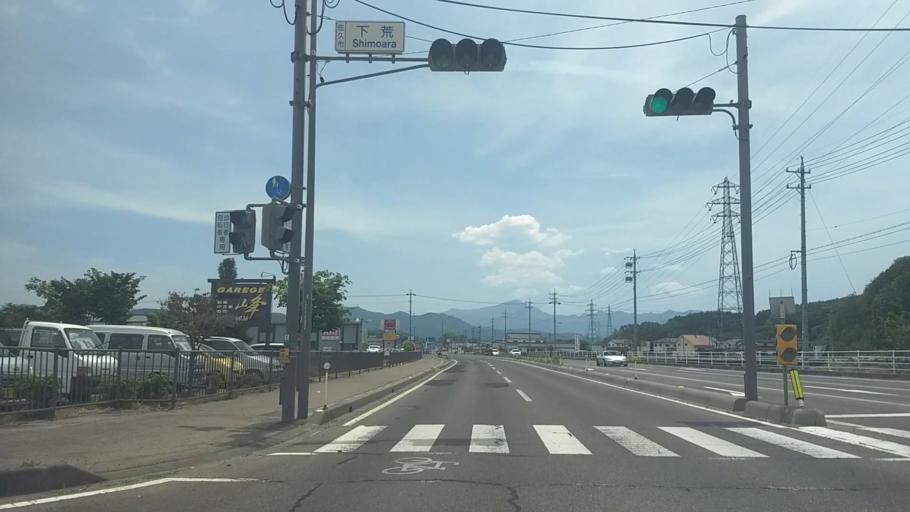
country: JP
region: Nagano
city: Saku
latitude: 36.2010
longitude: 138.4712
